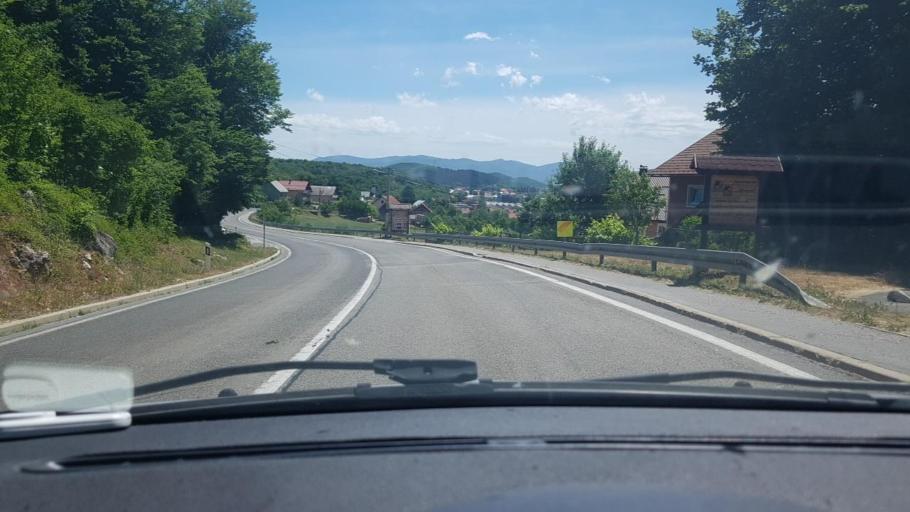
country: HR
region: Licko-Senjska
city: Otocac
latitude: 44.8742
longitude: 15.2095
